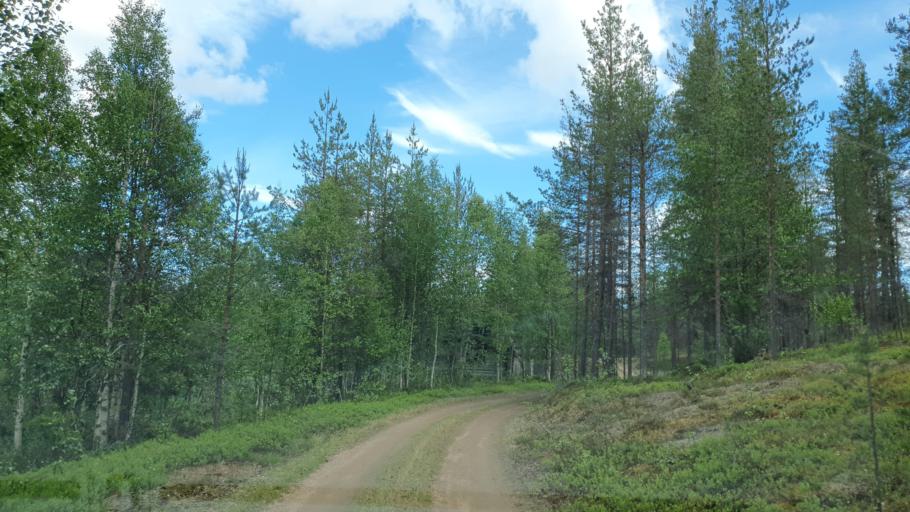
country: FI
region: Lapland
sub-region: Tunturi-Lappi
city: Kolari
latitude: 67.5357
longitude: 23.9178
